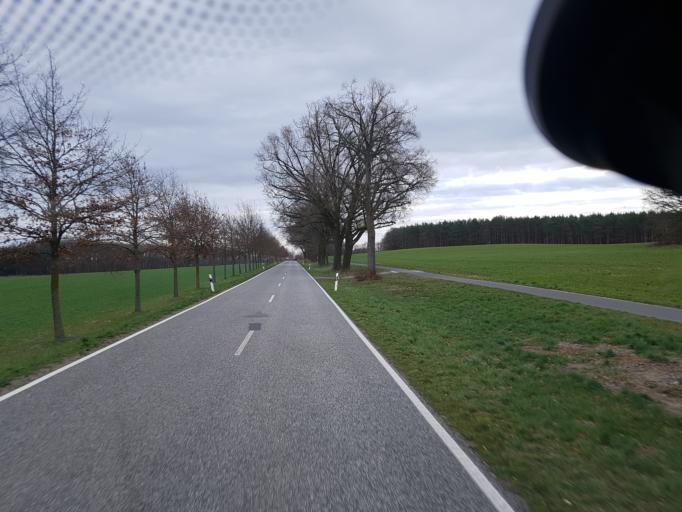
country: DE
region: Brandenburg
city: Mixdorf
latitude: 52.1961
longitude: 14.3295
